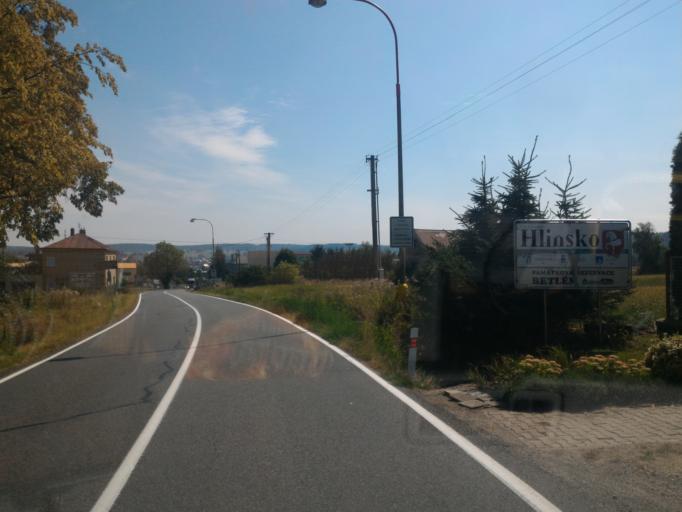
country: CZ
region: Pardubicky
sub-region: Okres Chrudim
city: Hlinsko
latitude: 49.7626
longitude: 15.8903
